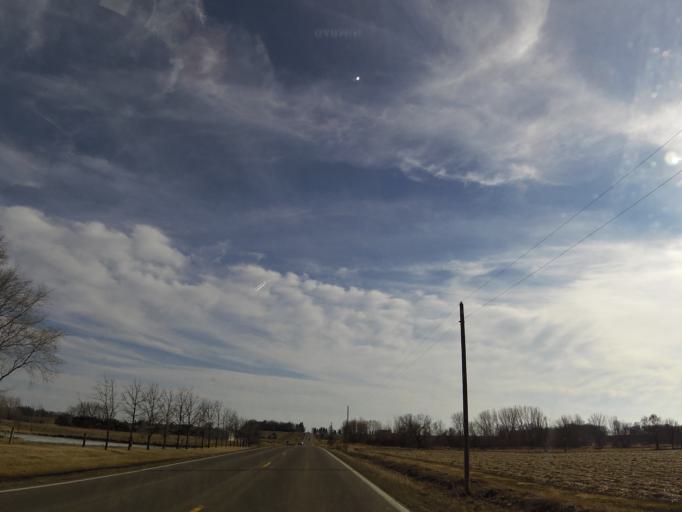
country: US
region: Minnesota
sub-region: Rice County
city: Northfield
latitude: 44.5387
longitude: -93.2010
